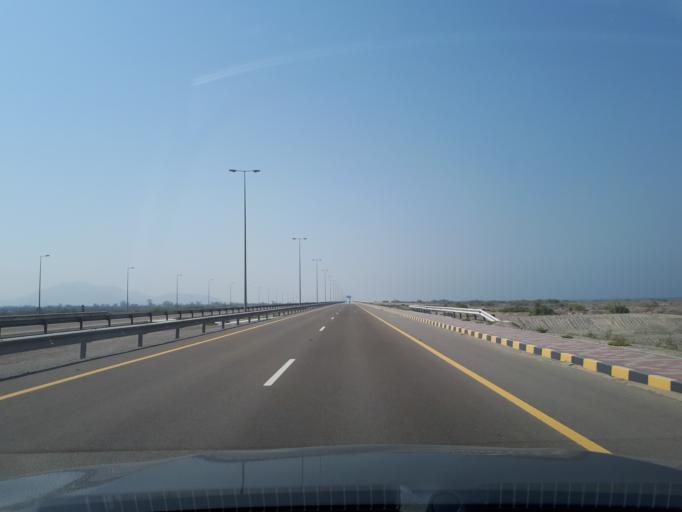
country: AE
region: Al Fujayrah
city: Al Fujayrah
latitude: 24.9340
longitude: 56.3836
